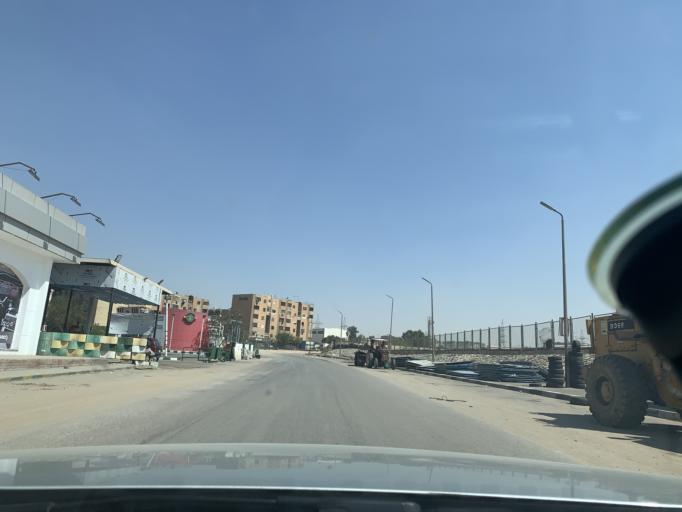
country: EG
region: Muhafazat al Qahirah
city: Cairo
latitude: 30.0455
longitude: 31.3550
